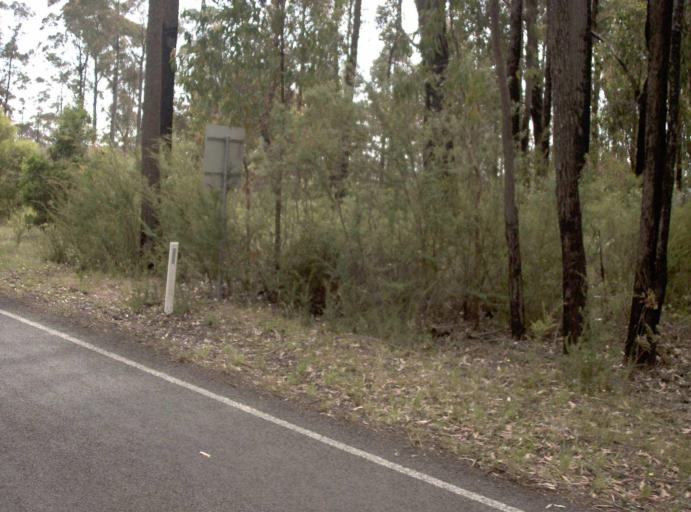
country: AU
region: Victoria
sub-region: Latrobe
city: Morwell
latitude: -38.0607
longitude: 146.4248
